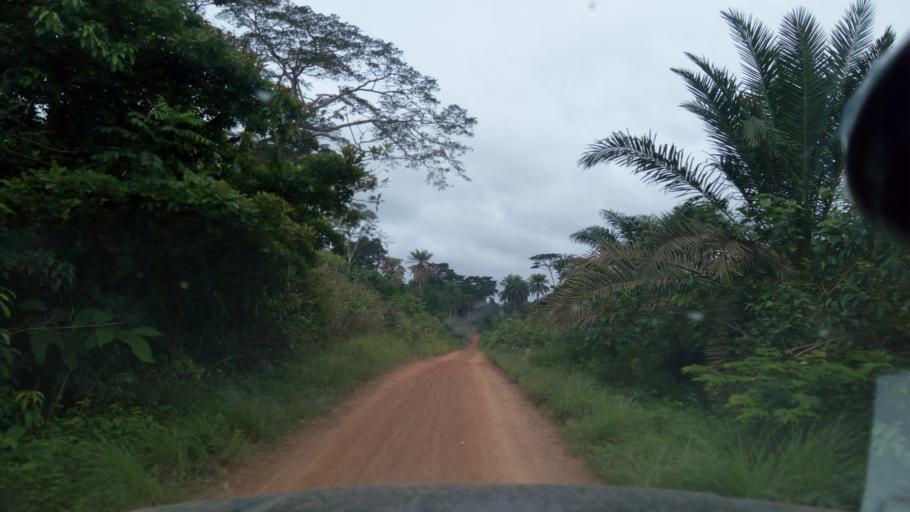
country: SL
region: Eastern Province
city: Kenema
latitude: 7.7380
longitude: -11.2102
